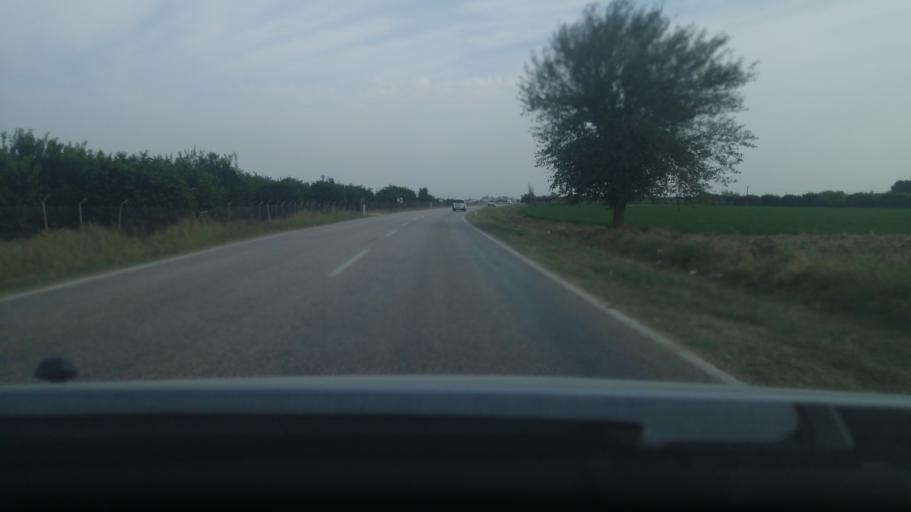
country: TR
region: Adana
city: Kozan
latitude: 37.3649
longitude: 35.8599
